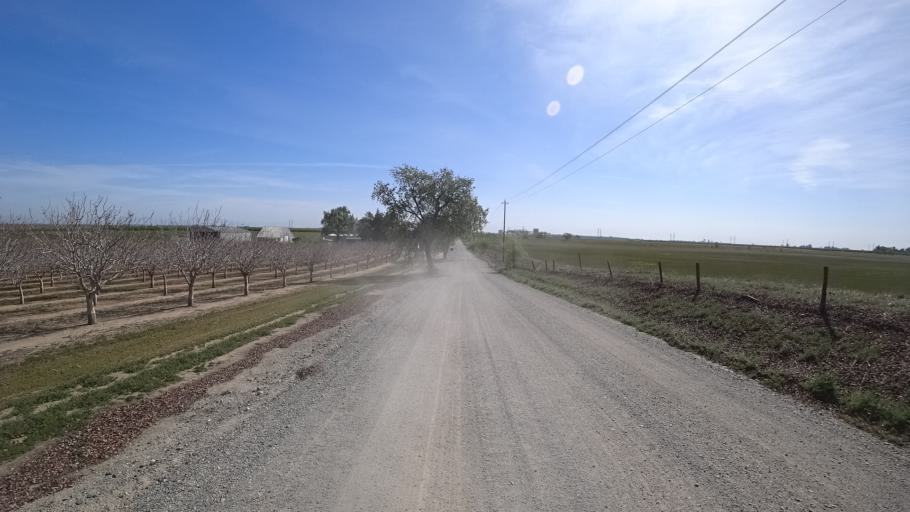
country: US
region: California
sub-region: Glenn County
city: Willows
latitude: 39.5388
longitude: -122.2766
